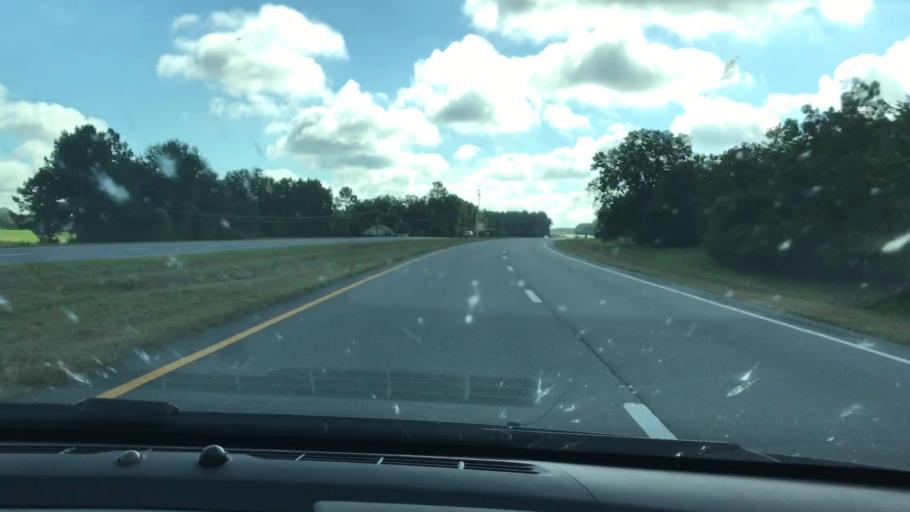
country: US
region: Georgia
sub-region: Worth County
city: Sylvester
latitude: 31.5530
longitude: -83.9508
